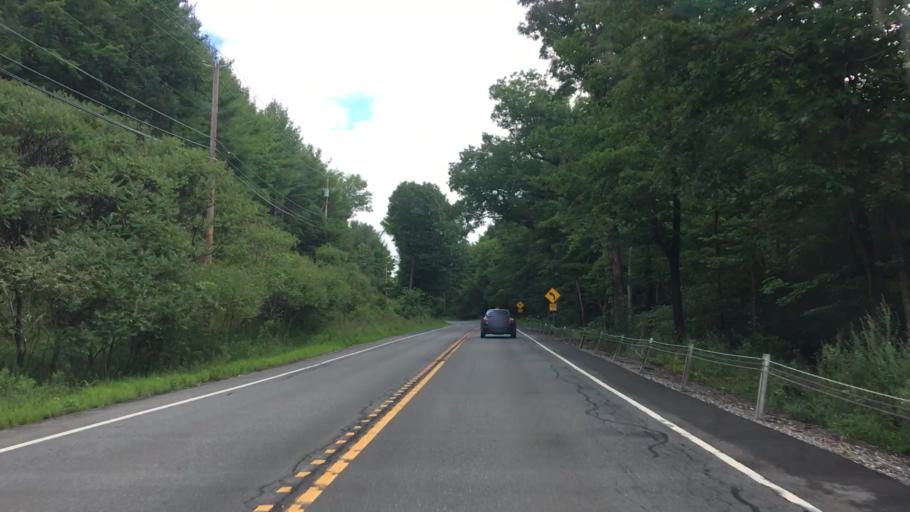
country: US
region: New York
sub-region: Rensselaer County
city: Poestenkill
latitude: 42.8245
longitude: -73.5001
